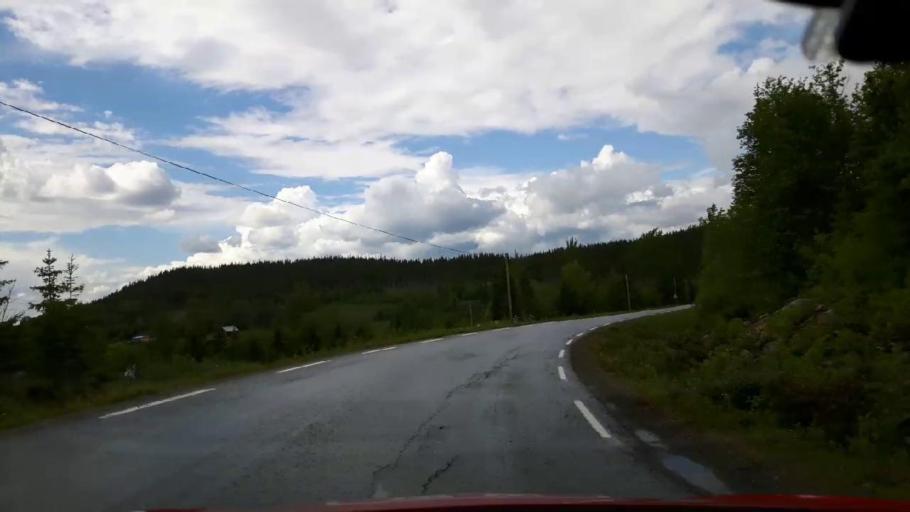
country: NO
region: Nord-Trondelag
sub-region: Lierne
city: Sandvika
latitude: 64.1000
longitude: 14.0251
